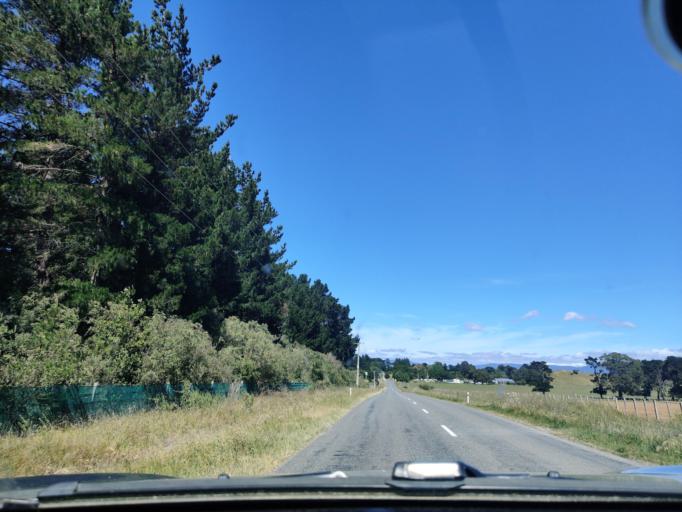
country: NZ
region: Wellington
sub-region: South Wairarapa District
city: Waipawa
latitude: -41.2258
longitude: 175.3485
